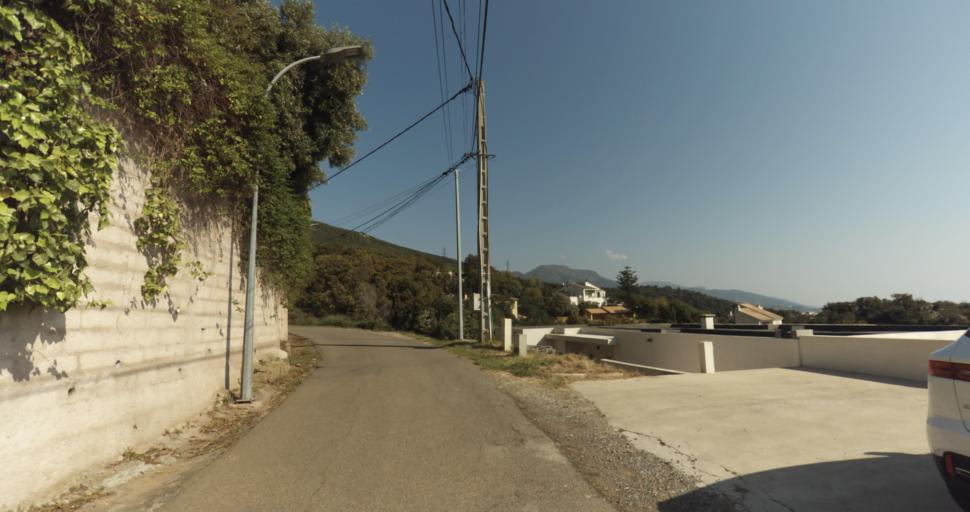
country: FR
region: Corsica
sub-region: Departement de la Haute-Corse
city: Biguglia
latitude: 42.6300
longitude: 9.4185
